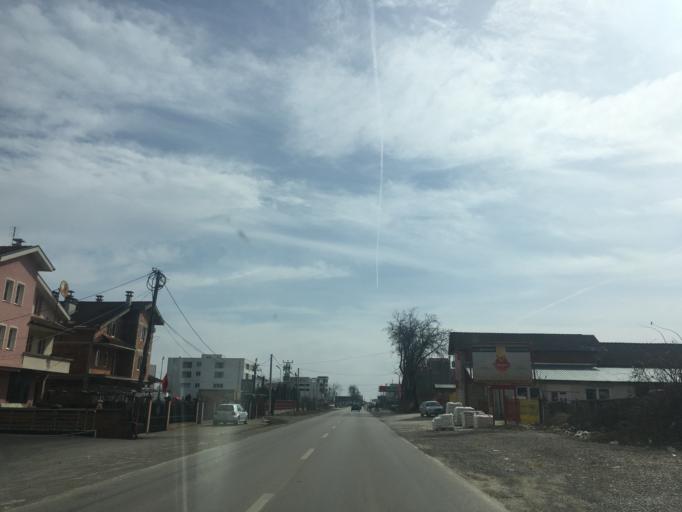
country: XK
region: Pec
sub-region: Komuna e Pejes
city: Peje
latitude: 42.6381
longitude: 20.2976
